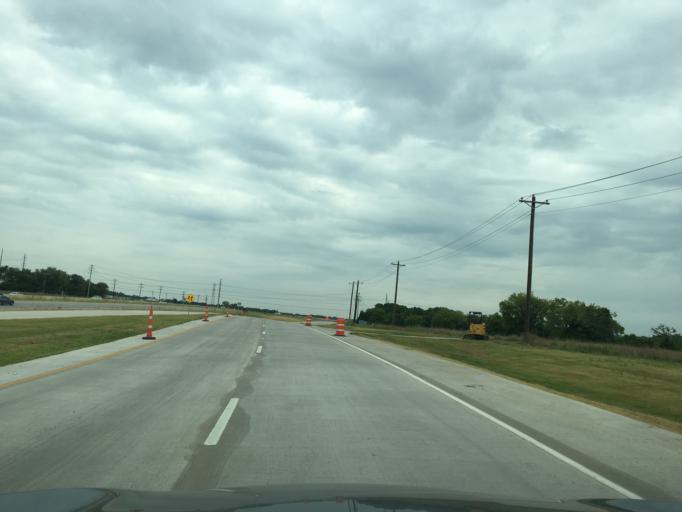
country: US
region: Texas
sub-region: Collin County
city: Melissa
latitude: 33.3107
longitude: -96.5902
